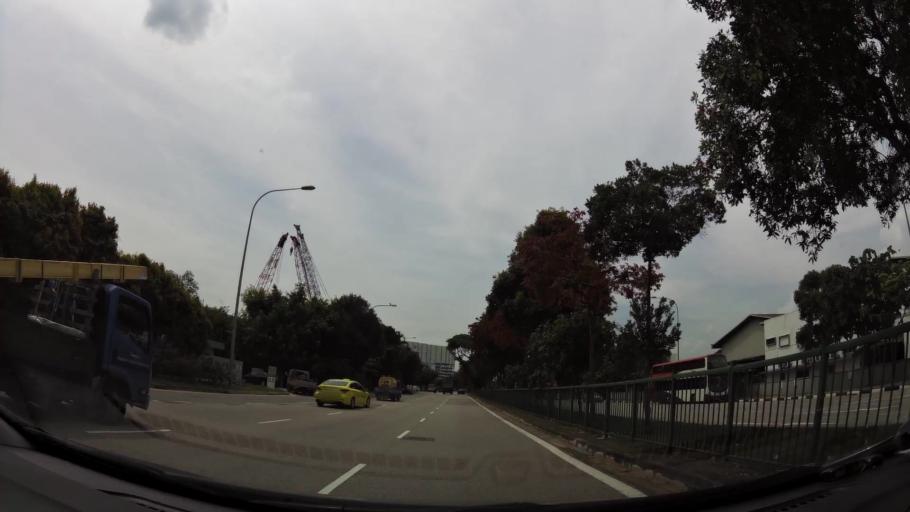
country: SG
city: Singapore
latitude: 1.3141
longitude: 103.7071
